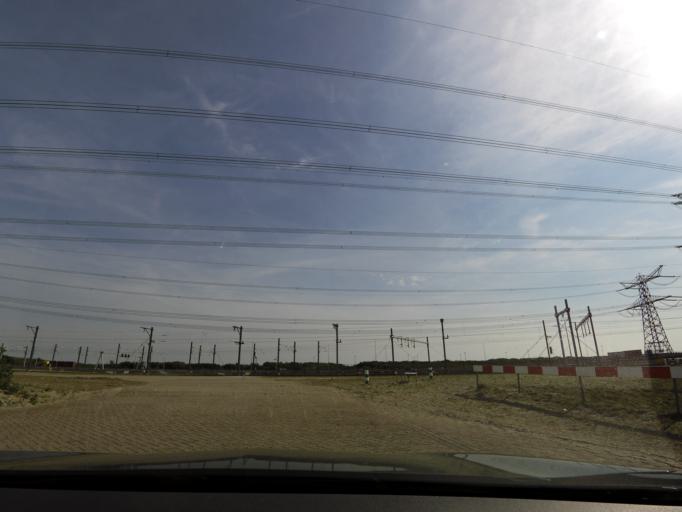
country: NL
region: South Holland
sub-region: Gemeente Rotterdam
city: Hoek van Holland
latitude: 51.9290
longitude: 4.0407
